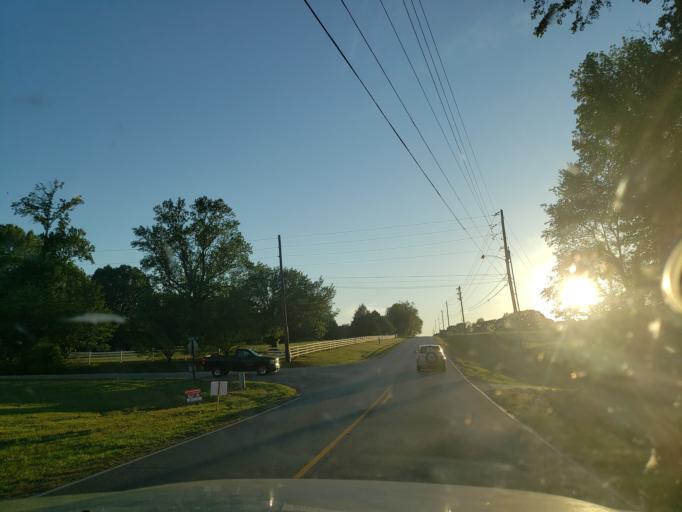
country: US
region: Alabama
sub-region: Madison County
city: Hazel Green
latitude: 34.9322
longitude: -86.5349
